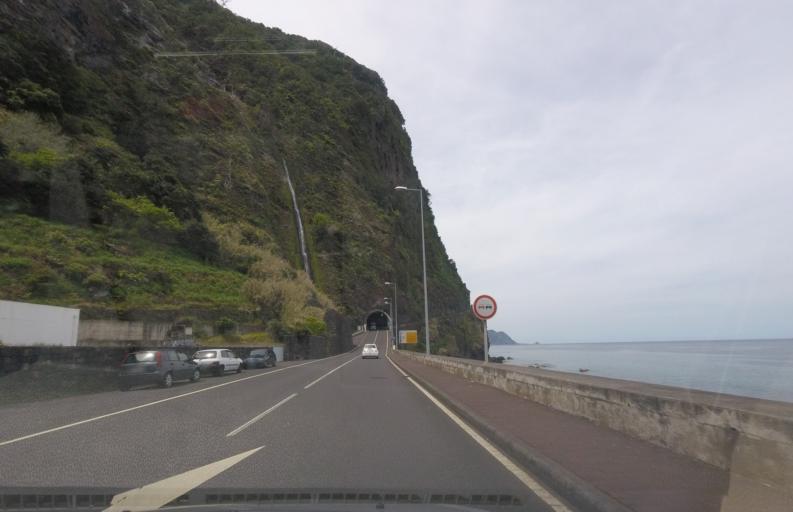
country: PT
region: Madeira
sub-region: Sao Vicente
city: Sao Vicente
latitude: 32.8096
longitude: -17.0584
